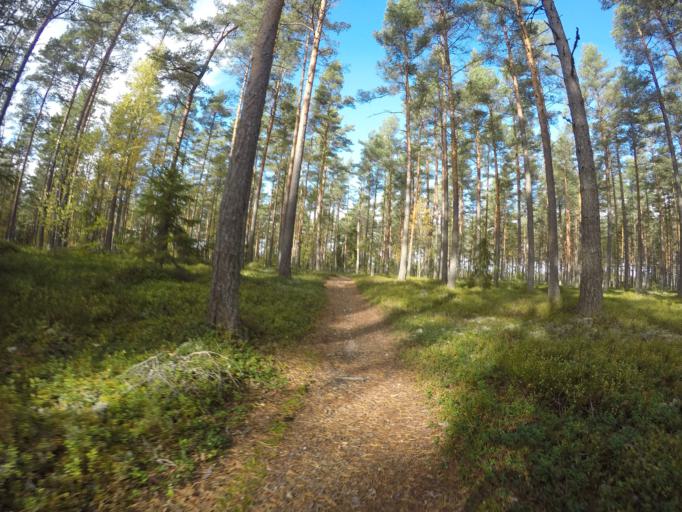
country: SE
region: Vaestmanland
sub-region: Kungsors Kommun
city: Kungsoer
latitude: 59.3256
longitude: 16.1130
